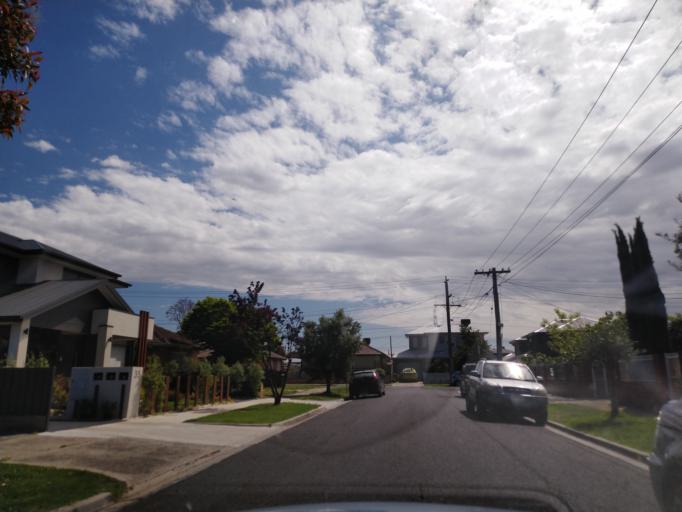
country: AU
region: Victoria
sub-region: Hobsons Bay
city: Altona North
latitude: -37.8289
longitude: 144.8533
